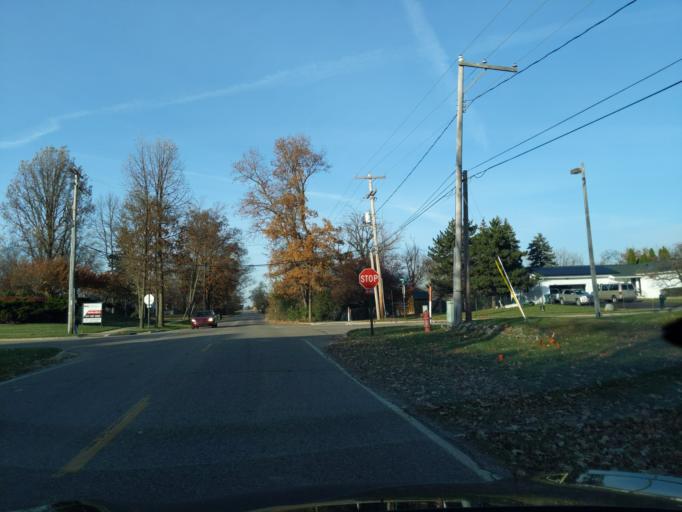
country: US
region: Michigan
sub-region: Ingham County
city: East Lansing
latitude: 42.7654
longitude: -84.5084
